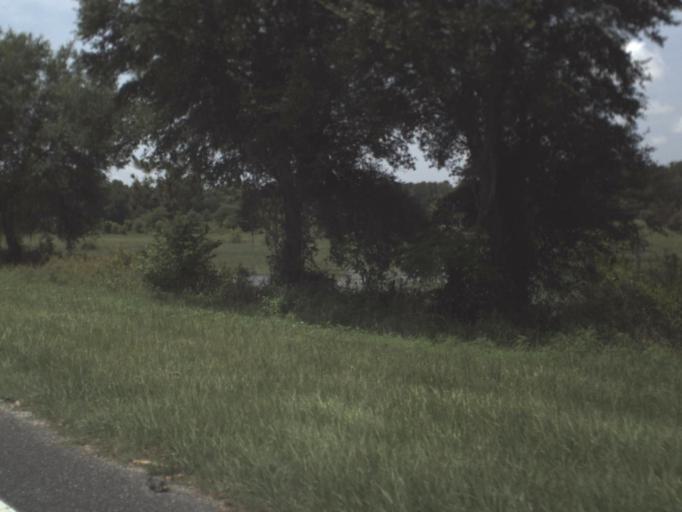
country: US
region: Florida
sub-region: Taylor County
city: Perry
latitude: 30.0551
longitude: -83.5528
